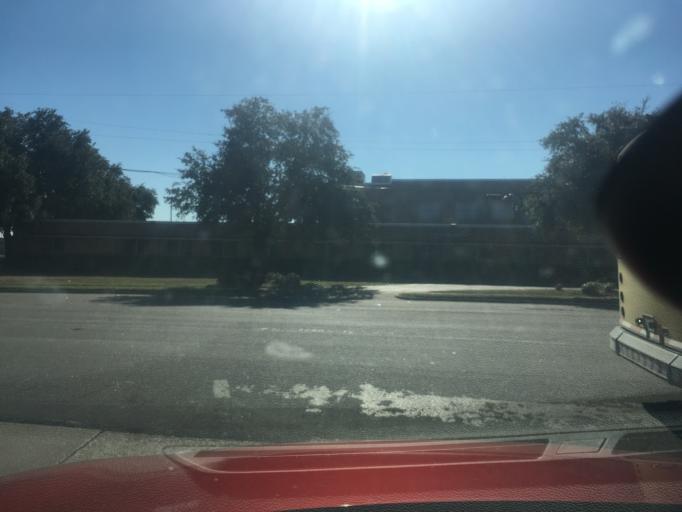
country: US
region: Texas
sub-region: Dallas County
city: Cockrell Hill
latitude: 32.7055
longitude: -96.8351
